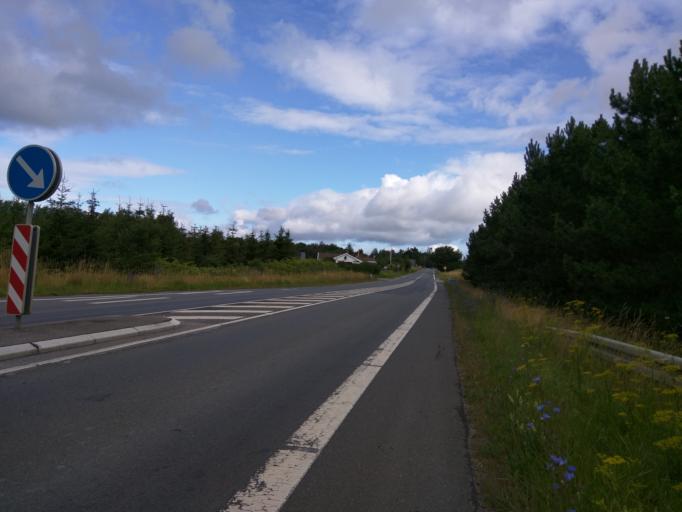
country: DK
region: Zealand
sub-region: Kalundborg Kommune
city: Svebolle
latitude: 55.6705
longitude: 11.2975
